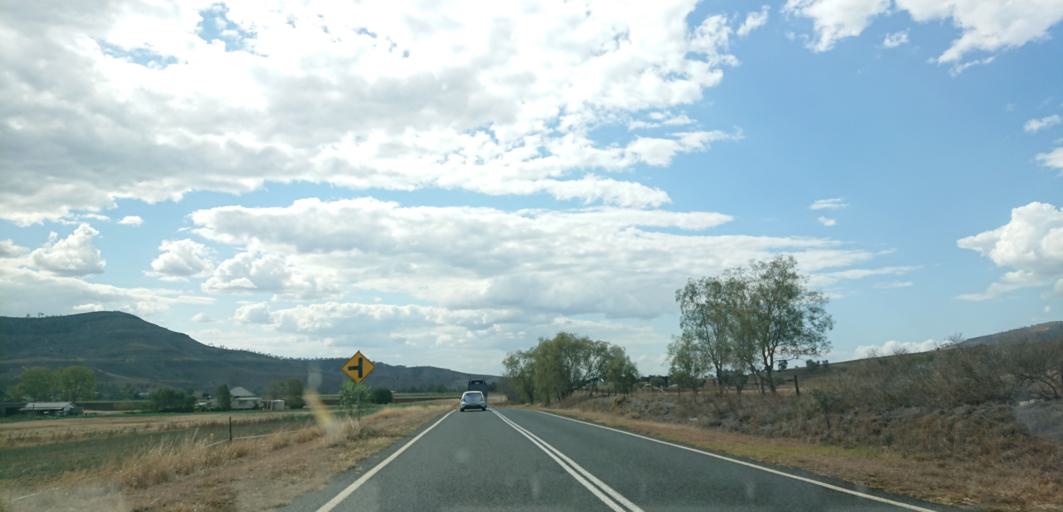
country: AU
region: Queensland
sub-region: Lockyer Valley
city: Gatton
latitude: -27.6735
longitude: 152.1550
